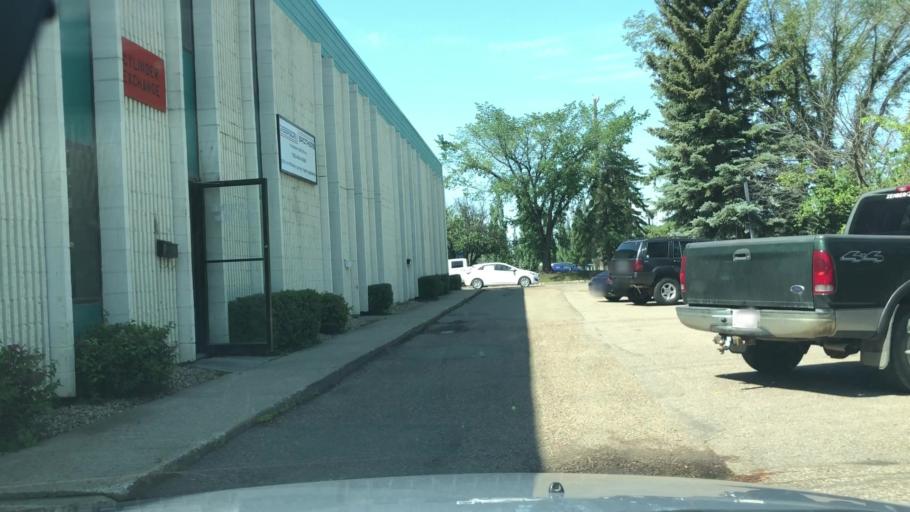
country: CA
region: Alberta
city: St. Albert
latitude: 53.5734
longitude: -113.5961
